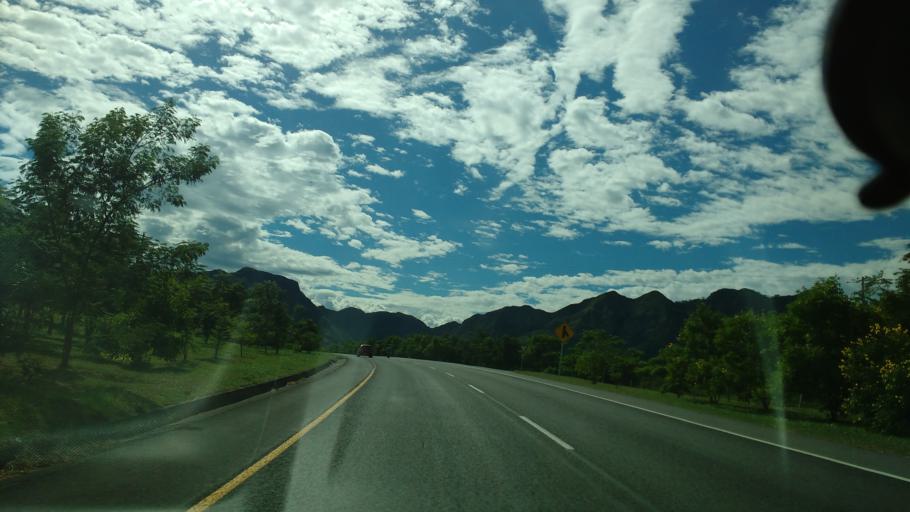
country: CO
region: Tolima
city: Valle de San Juan
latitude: 4.2718
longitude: -75.0001
